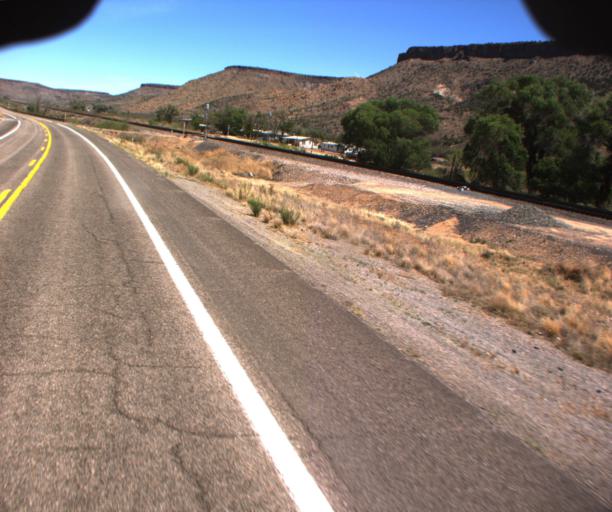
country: US
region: Arizona
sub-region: Mohave County
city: Peach Springs
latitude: 35.3857
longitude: -113.6600
